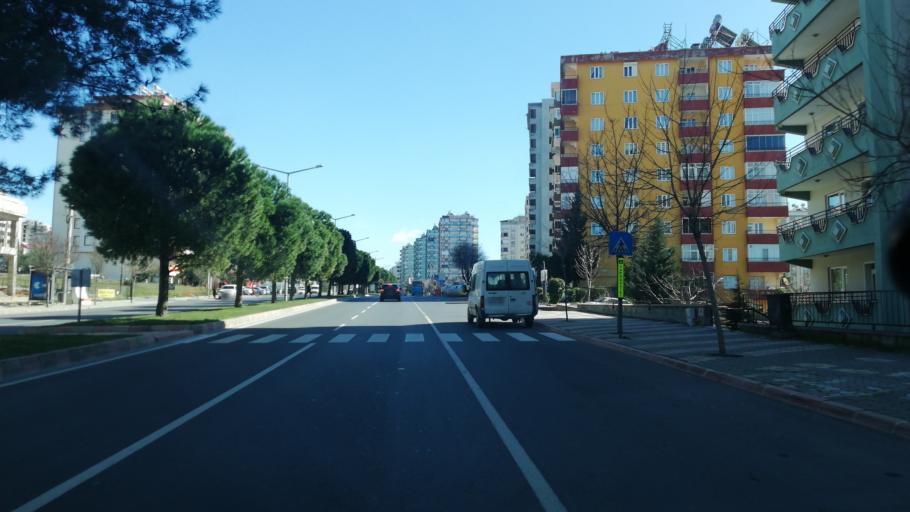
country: TR
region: Kahramanmaras
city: Kahramanmaras
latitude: 37.5828
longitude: 36.8825
